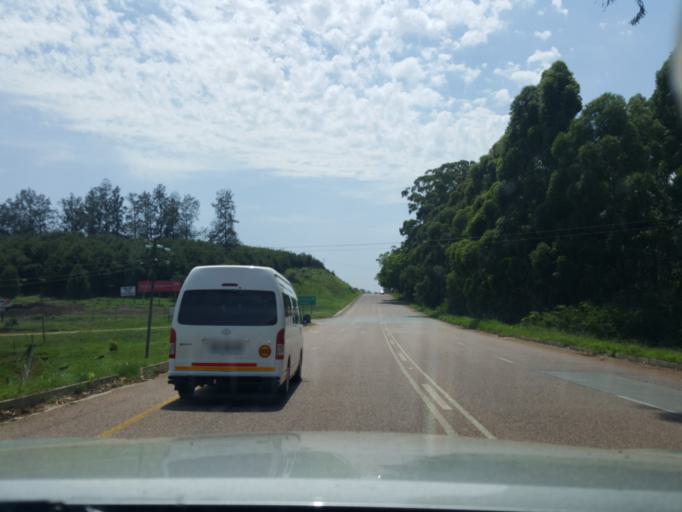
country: ZA
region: Mpumalanga
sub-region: Ehlanzeni District
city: White River
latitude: -25.1163
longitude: 31.0345
